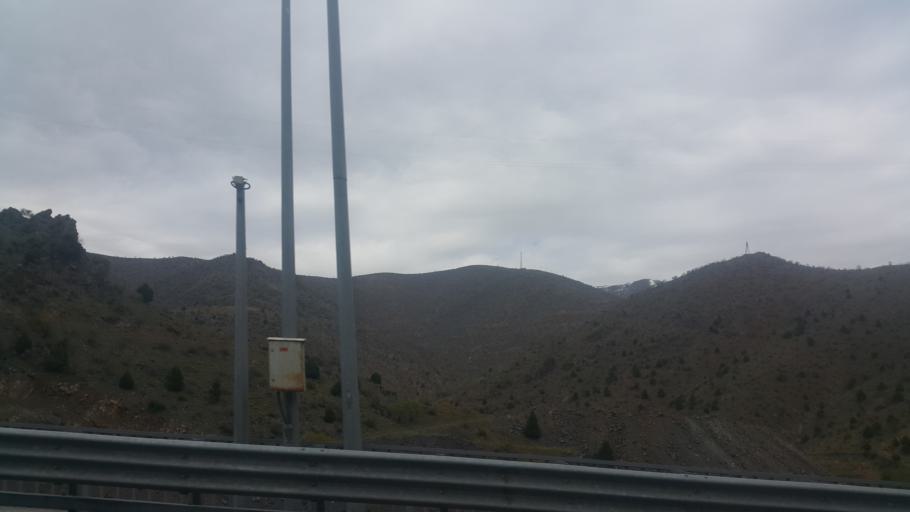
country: TR
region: Nigde
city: Ciftehan
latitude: 37.5571
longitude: 34.7661
